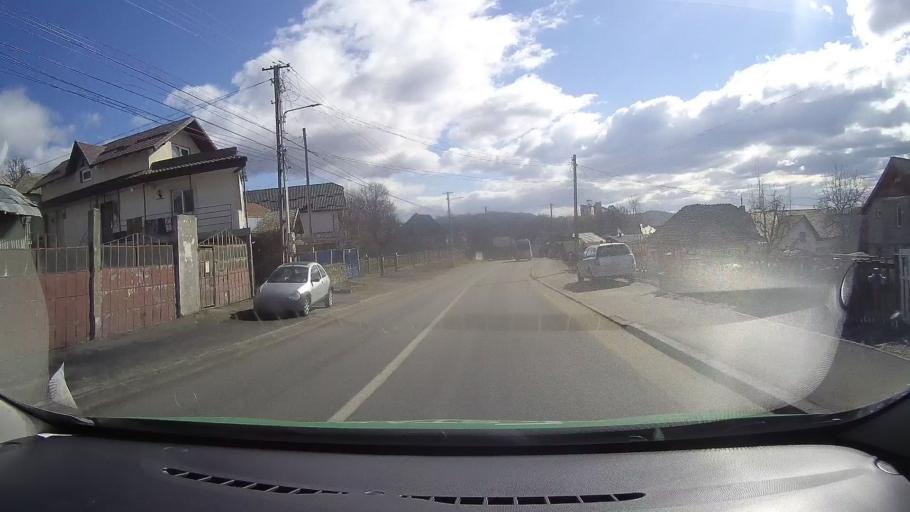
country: RO
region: Dambovita
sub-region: Comuna Fieni
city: Fieni
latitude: 45.1296
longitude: 25.4103
